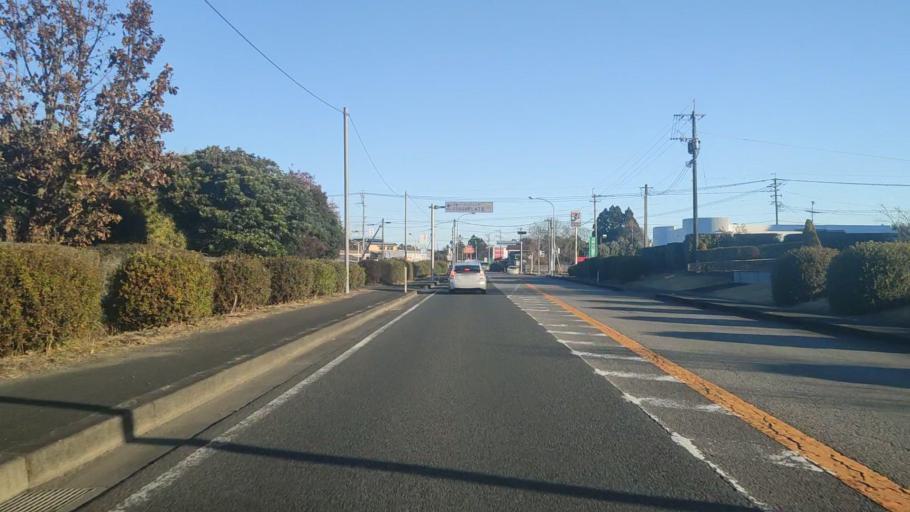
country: JP
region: Miyazaki
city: Takanabe
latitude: 32.1862
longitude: 131.5233
